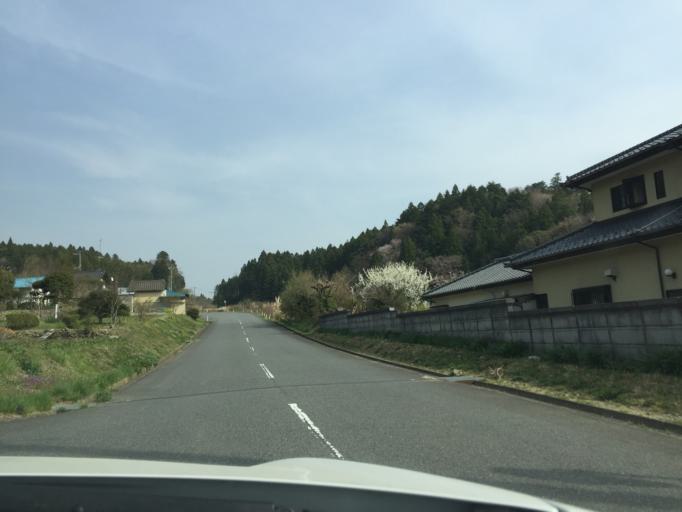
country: JP
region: Fukushima
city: Iwaki
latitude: 37.0257
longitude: 140.7594
